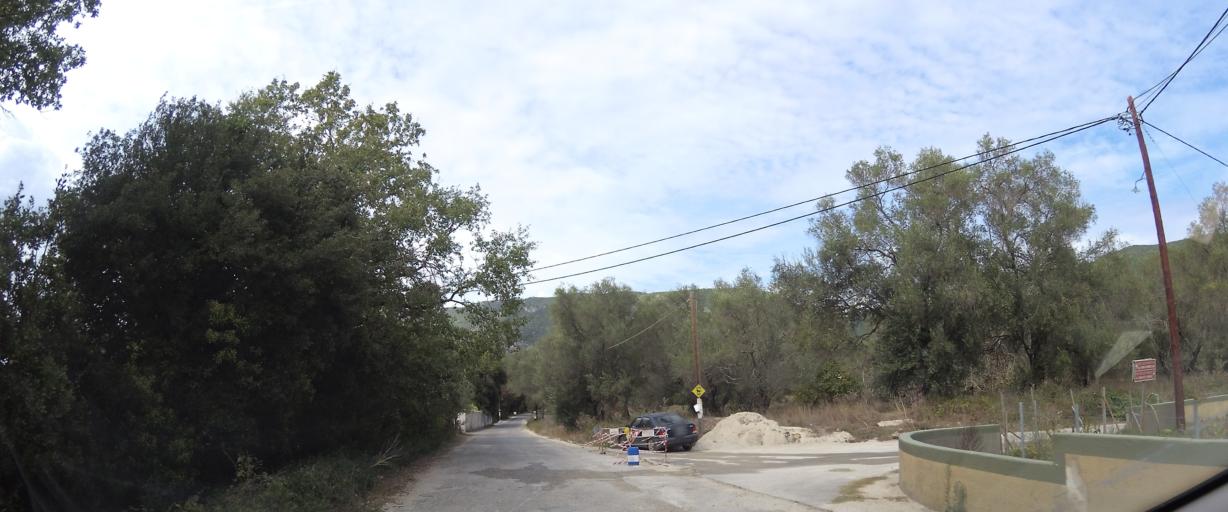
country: GR
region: Ionian Islands
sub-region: Nomos Kerkyras
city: Kontokali
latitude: 39.6973
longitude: 19.8045
